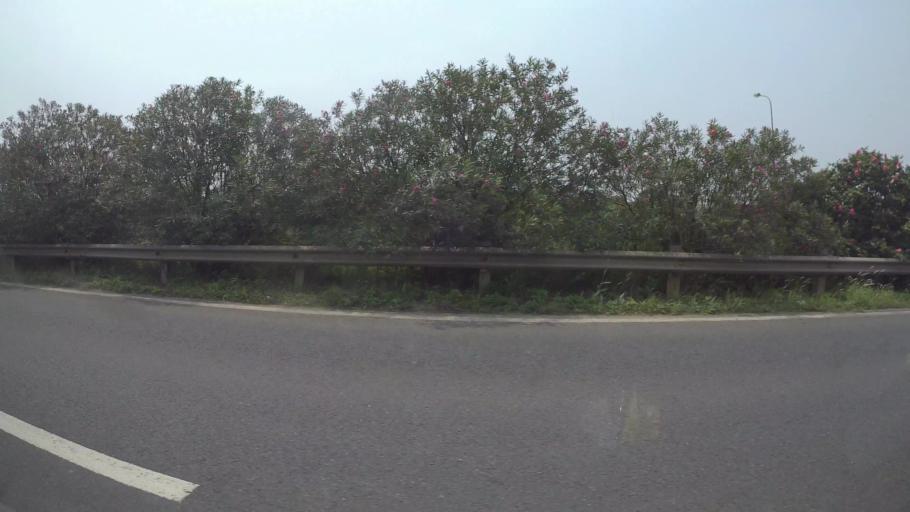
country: VN
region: Ha Noi
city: Quoc Oai
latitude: 21.0012
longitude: 105.6043
